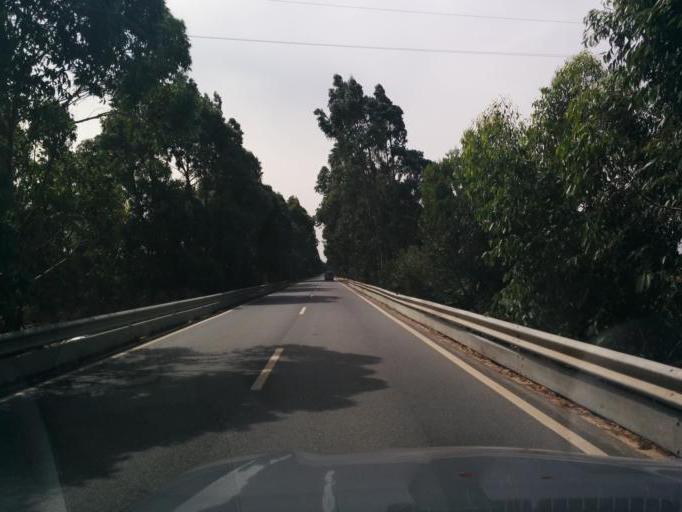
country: PT
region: Beja
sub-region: Odemira
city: Vila Nova de Milfontes
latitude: 37.6792
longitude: -8.7624
